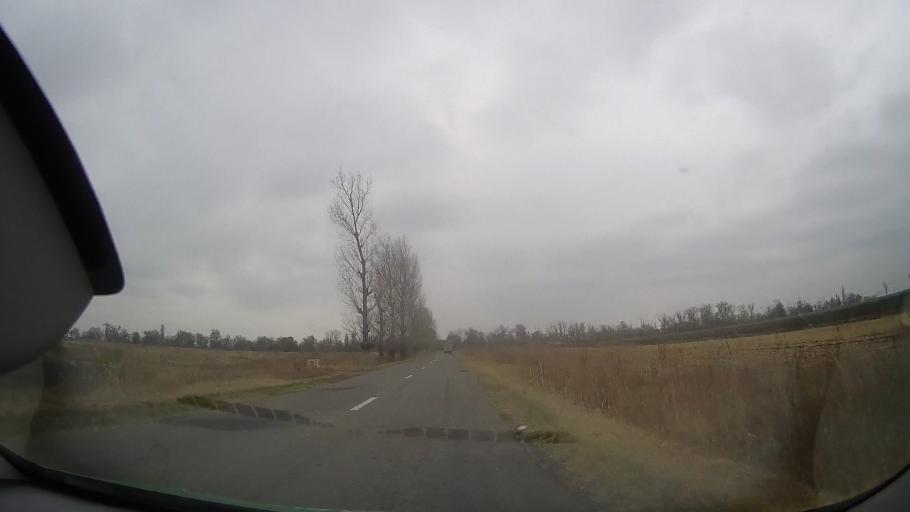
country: RO
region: Ialomita
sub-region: Comuna Garbovi
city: Garbovi
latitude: 44.7706
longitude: 26.7878
